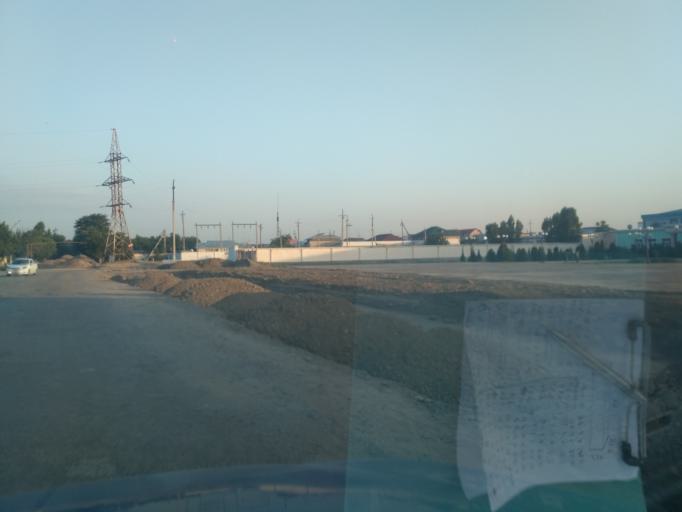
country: UZ
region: Sirdaryo
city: Guliston
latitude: 40.5049
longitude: 68.7683
